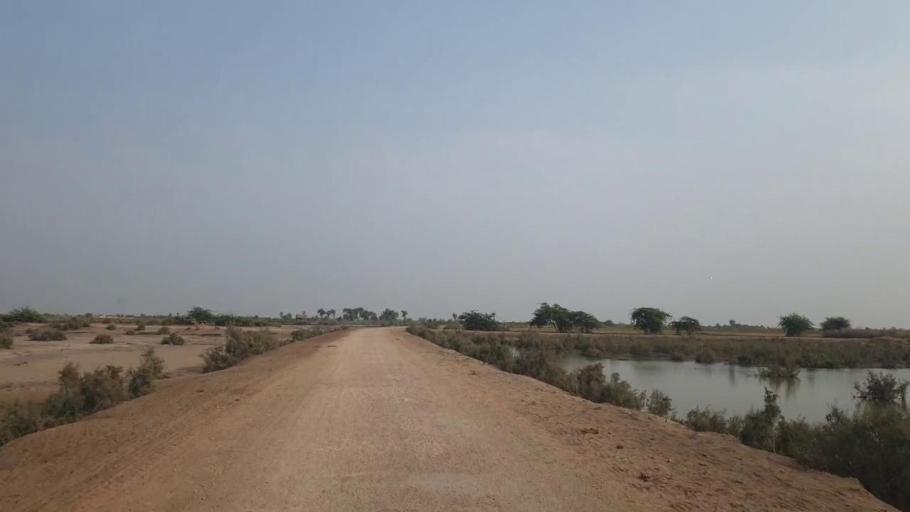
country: PK
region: Sindh
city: Badin
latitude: 24.6057
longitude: 68.6920
